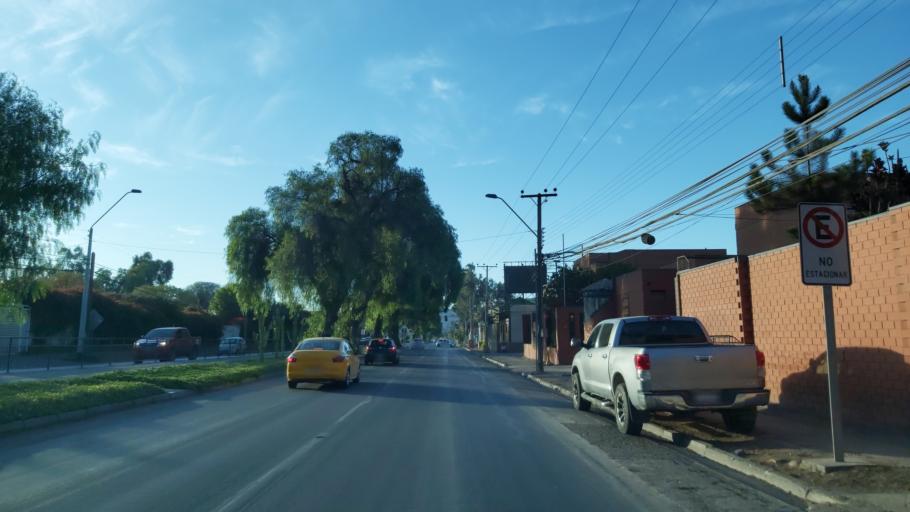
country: CL
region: Atacama
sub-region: Provincia de Copiapo
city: Copiapo
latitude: -27.3843
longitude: -70.3143
